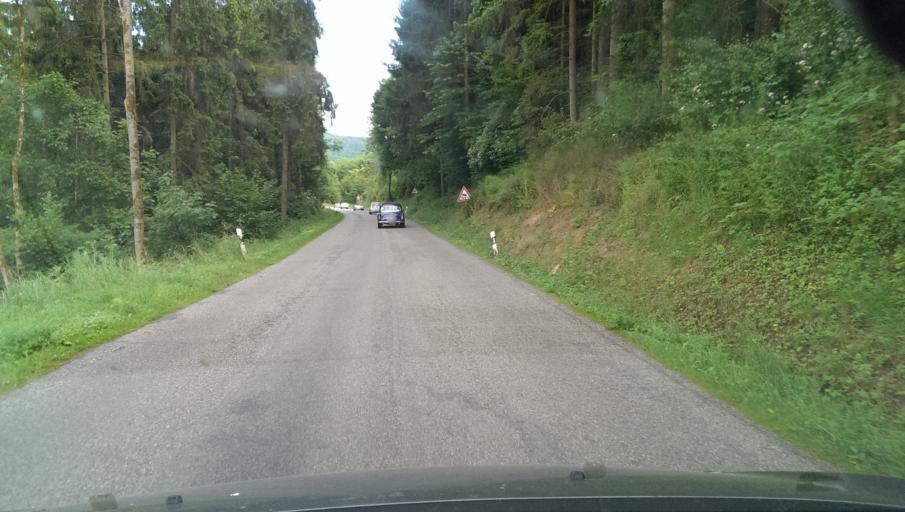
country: DE
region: Baden-Wuerttemberg
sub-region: Regierungsbezirk Stuttgart
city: Forchtenberg
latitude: 49.2813
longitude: 9.5647
